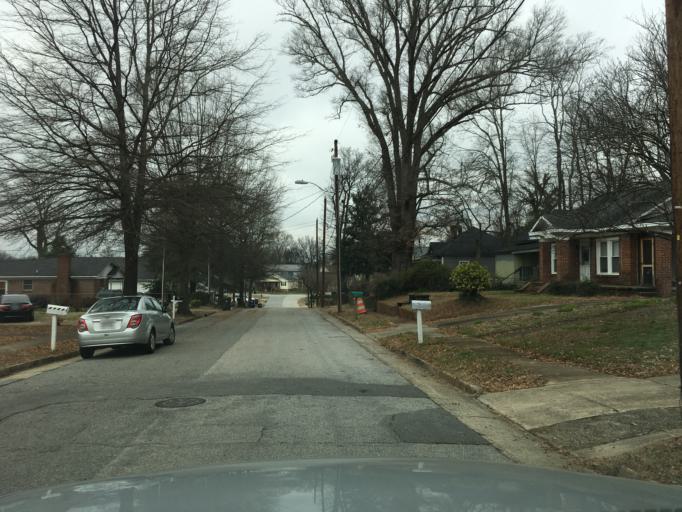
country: US
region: South Carolina
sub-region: Greenville County
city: Greenville
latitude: 34.8568
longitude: -82.4096
